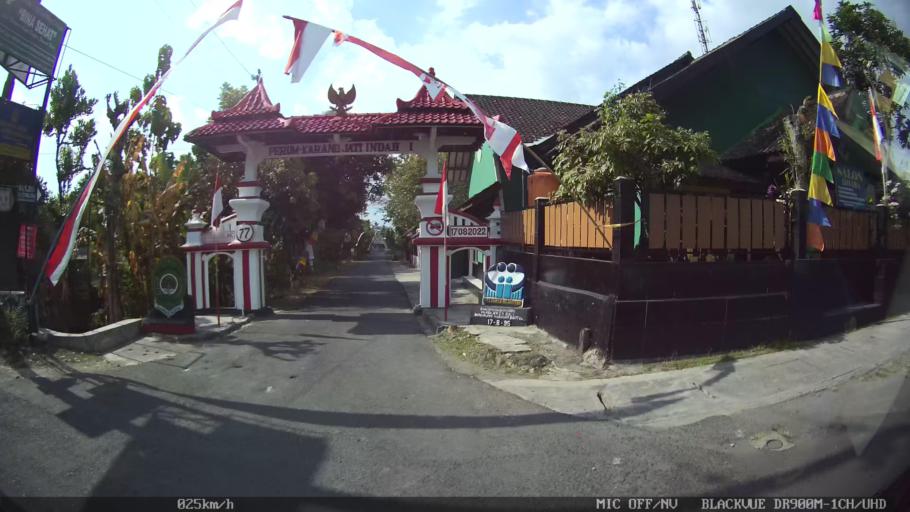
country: ID
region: Daerah Istimewa Yogyakarta
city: Kasihan
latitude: -7.8377
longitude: 110.3160
